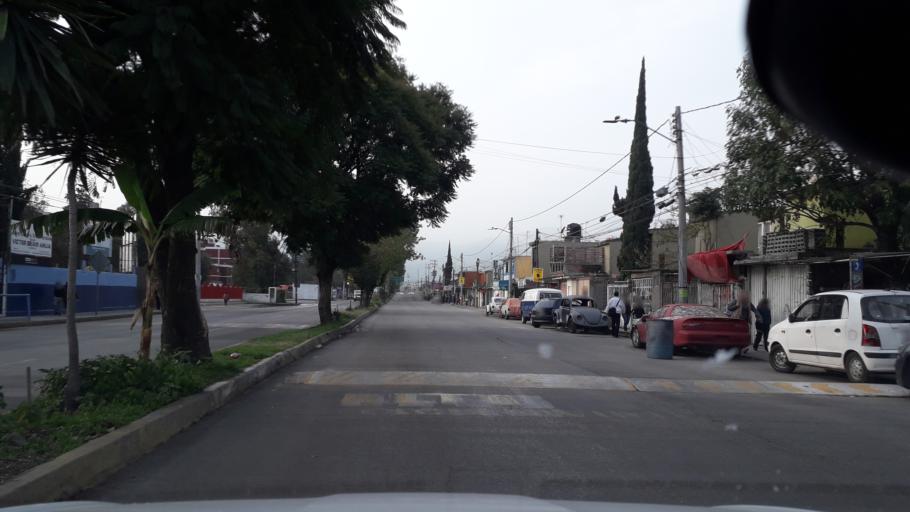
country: MX
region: Mexico
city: San Pablo de las Salinas
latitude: 19.6544
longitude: -99.0845
